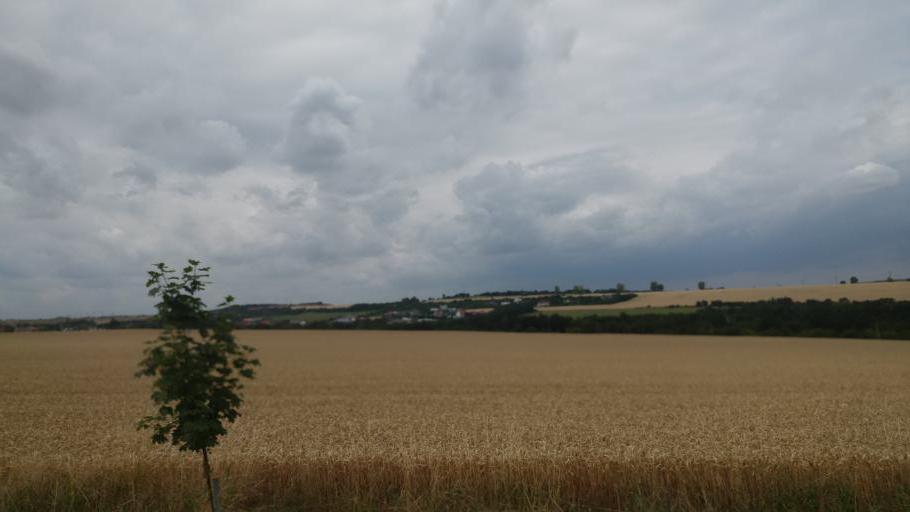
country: CZ
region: Central Bohemia
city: Horomerice
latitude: 50.1456
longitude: 14.3497
